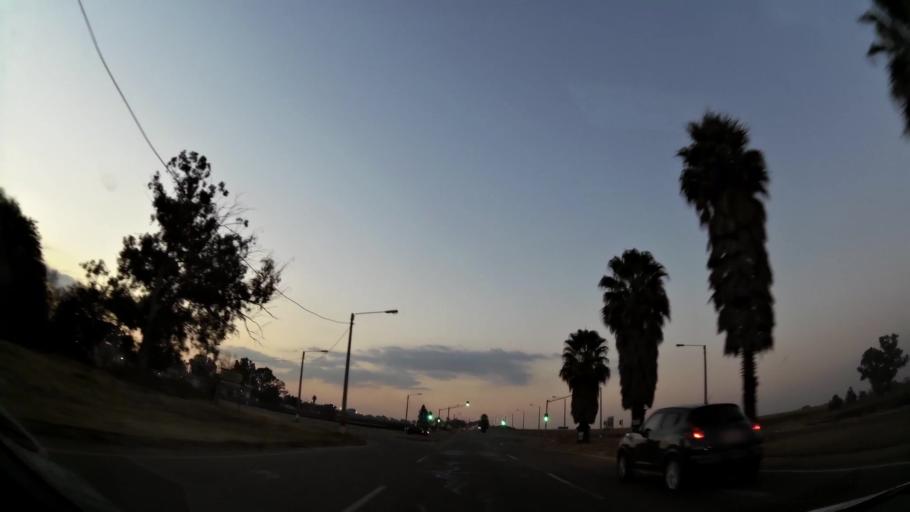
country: ZA
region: Gauteng
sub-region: Ekurhuleni Metropolitan Municipality
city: Springs
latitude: -26.3169
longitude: 28.4554
